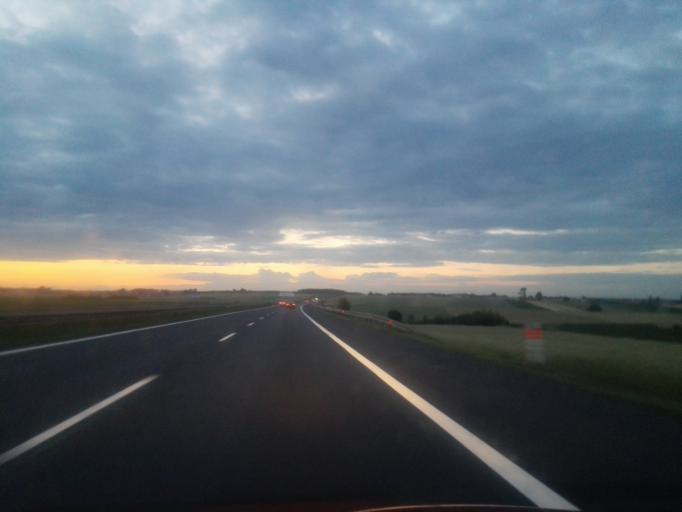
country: PL
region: Lodz Voivodeship
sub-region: Powiat piotrkowski
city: Grabica
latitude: 51.5189
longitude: 19.6001
